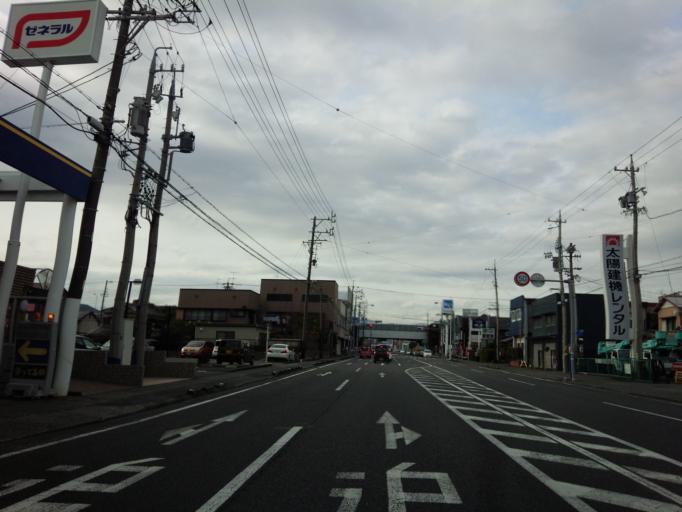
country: JP
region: Shizuoka
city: Shizuoka-shi
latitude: 34.9444
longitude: 138.3928
